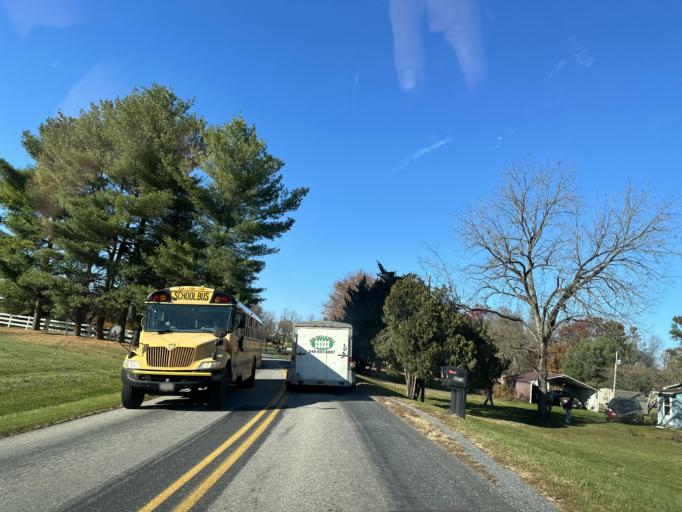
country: US
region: Virginia
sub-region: Rockingham County
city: Bridgewater
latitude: 38.4210
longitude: -79.0423
